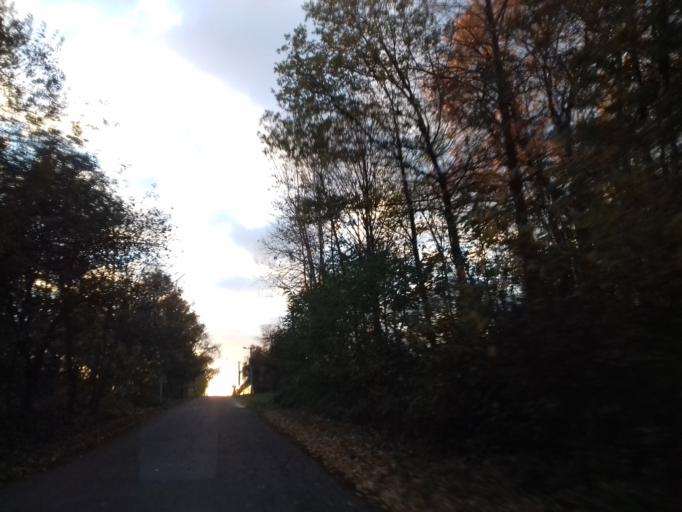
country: CZ
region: Pardubicky
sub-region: Okres Chrudim
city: Skutec
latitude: 49.8259
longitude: 15.9744
